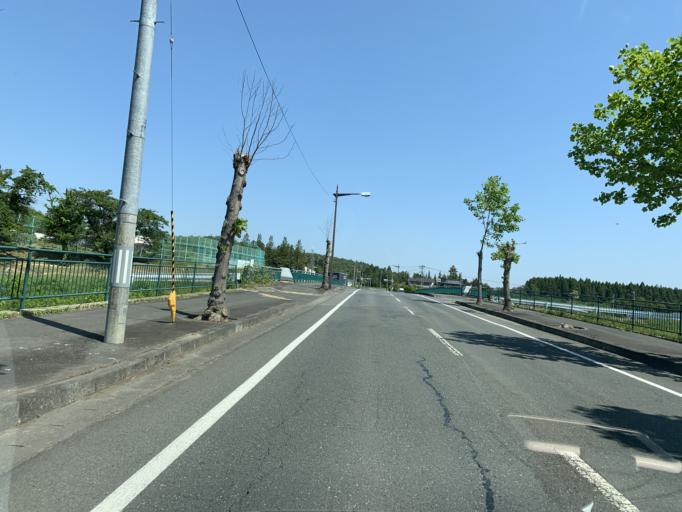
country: JP
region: Iwate
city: Kitakami
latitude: 39.2050
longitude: 141.0949
